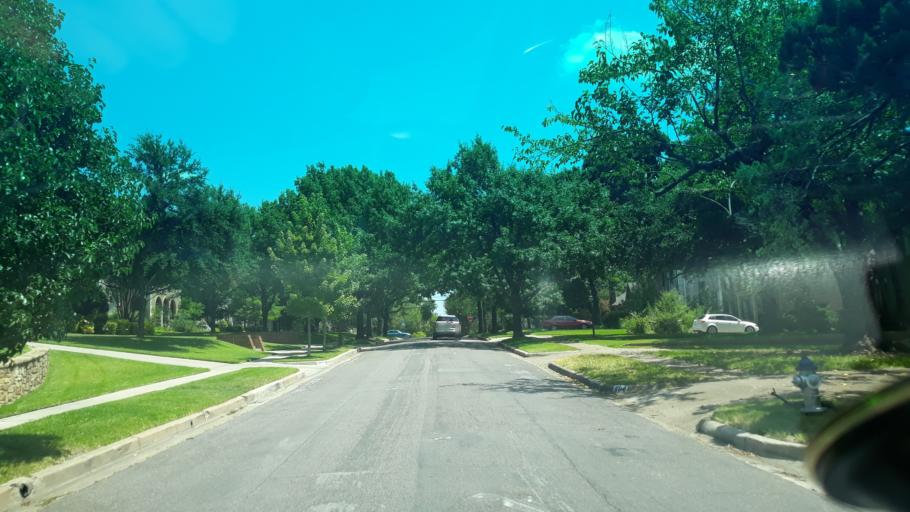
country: US
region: Texas
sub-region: Dallas County
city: Highland Park
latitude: 32.8203
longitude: -96.7391
